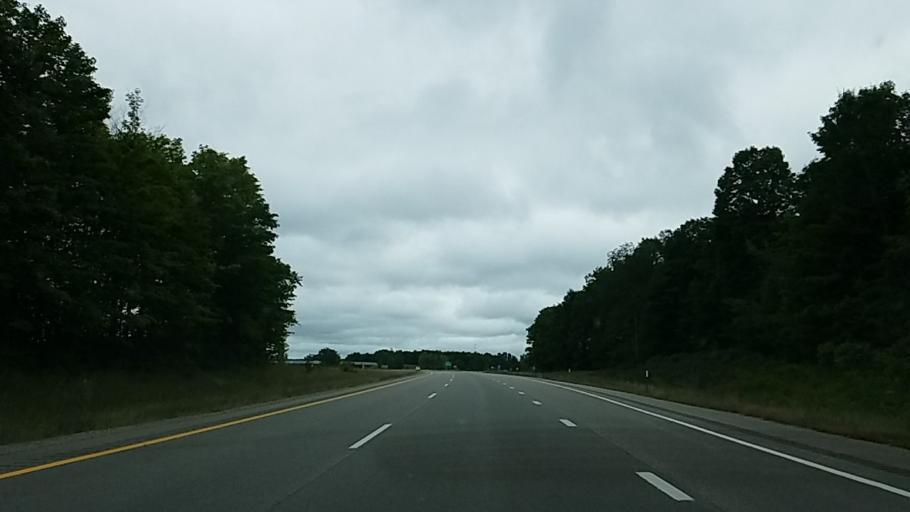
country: US
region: Michigan
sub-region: Otsego County
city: Gaylord
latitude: 45.1555
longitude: -84.6685
